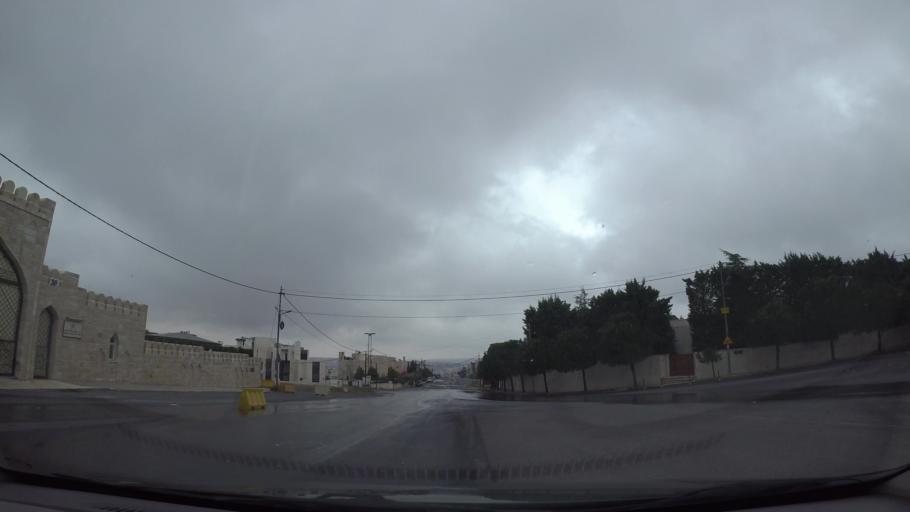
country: JO
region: Amman
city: Al Bunayyat ash Shamaliyah
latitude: 31.9445
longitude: 35.8831
